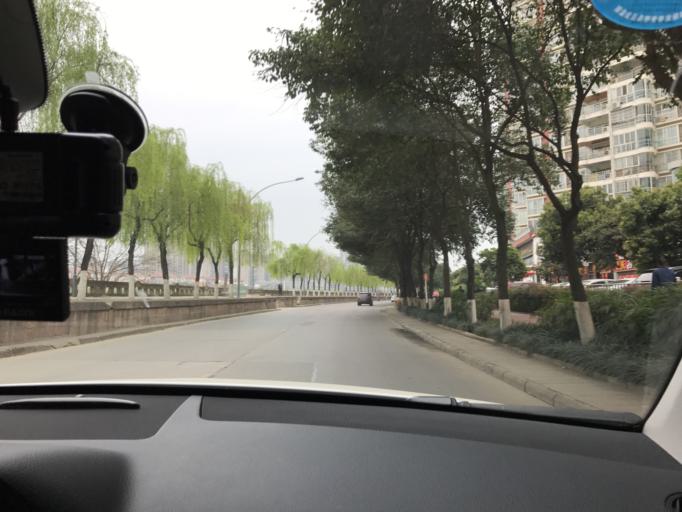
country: CN
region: Sichuan
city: Mianyang
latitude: 31.4524
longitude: 104.7117
